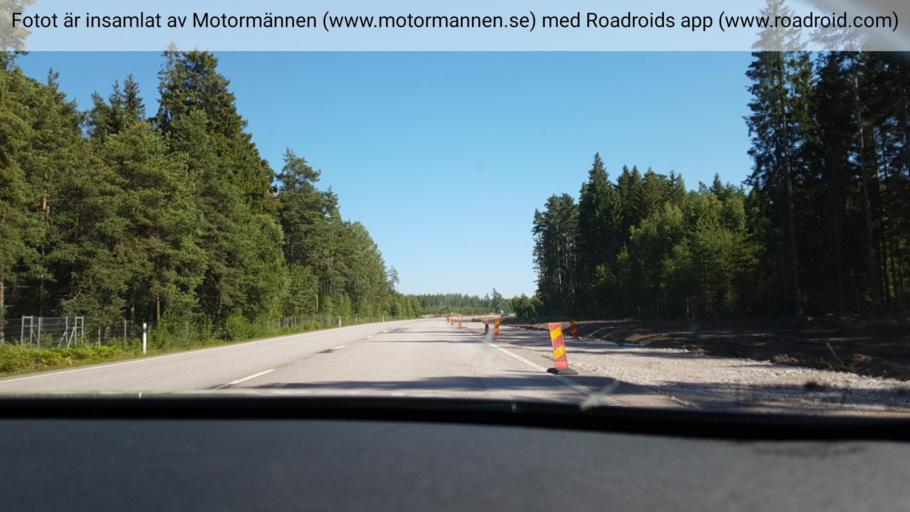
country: SE
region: Vaestra Goetaland
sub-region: Lidkopings Kommun
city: Lidkoping
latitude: 58.4826
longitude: 13.1971
